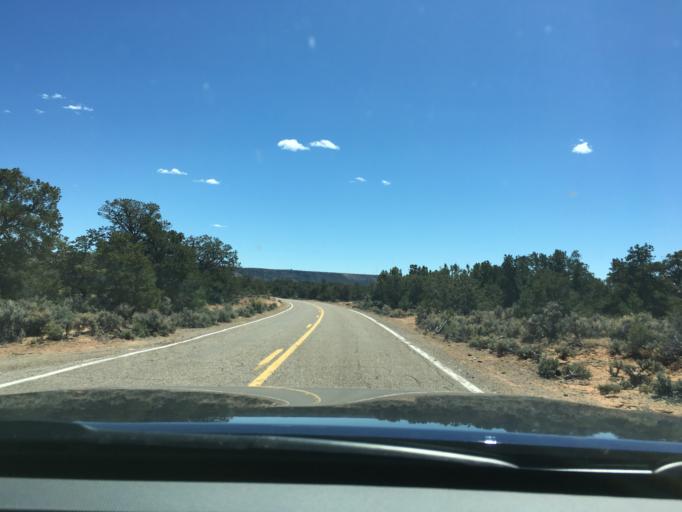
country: US
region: Arizona
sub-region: Navajo County
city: Kayenta
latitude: 36.5937
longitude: -110.4963
